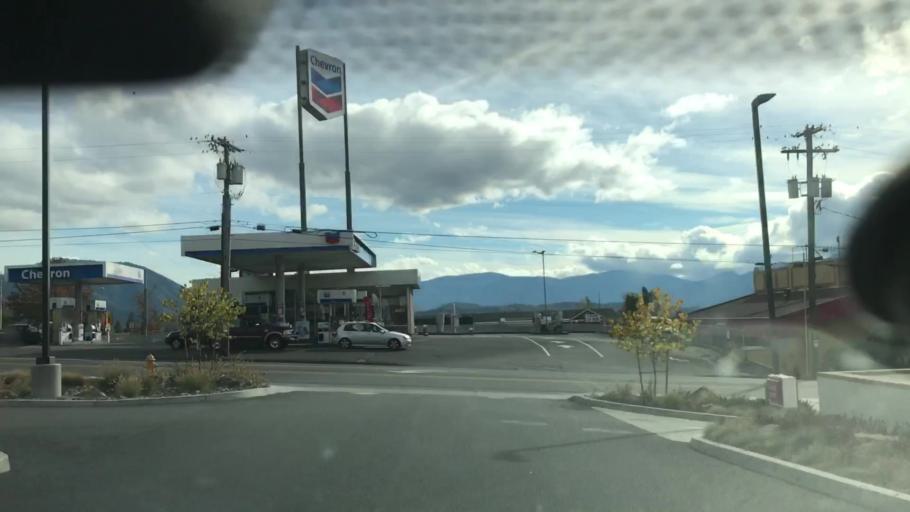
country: US
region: Oregon
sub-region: Josephine County
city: Grants Pass
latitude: 42.4626
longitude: -123.3213
